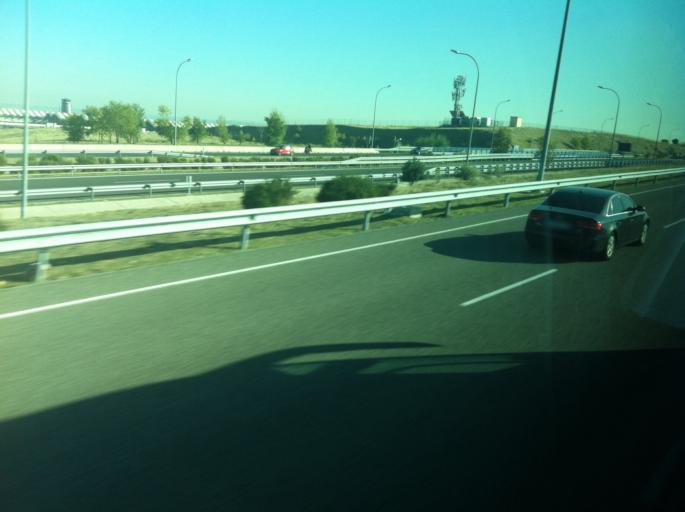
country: ES
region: Madrid
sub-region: Provincia de Madrid
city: Barajas de Madrid
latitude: 40.4970
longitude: -3.6025
